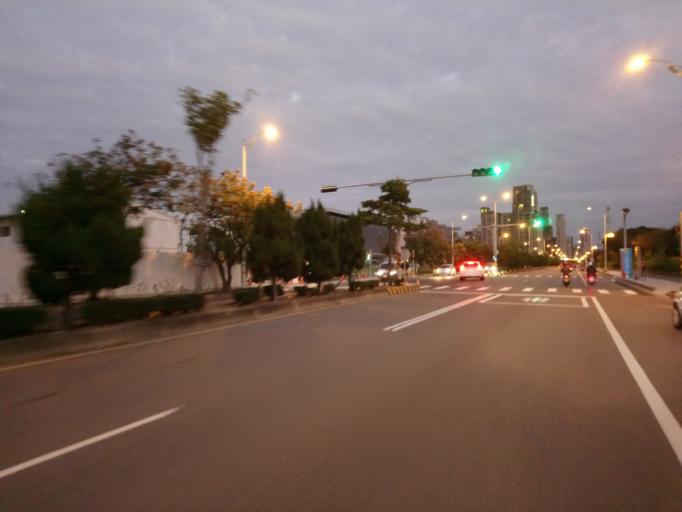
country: TW
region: Taiwan
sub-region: Hsinchu
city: Zhubei
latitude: 24.8229
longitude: 121.0026
